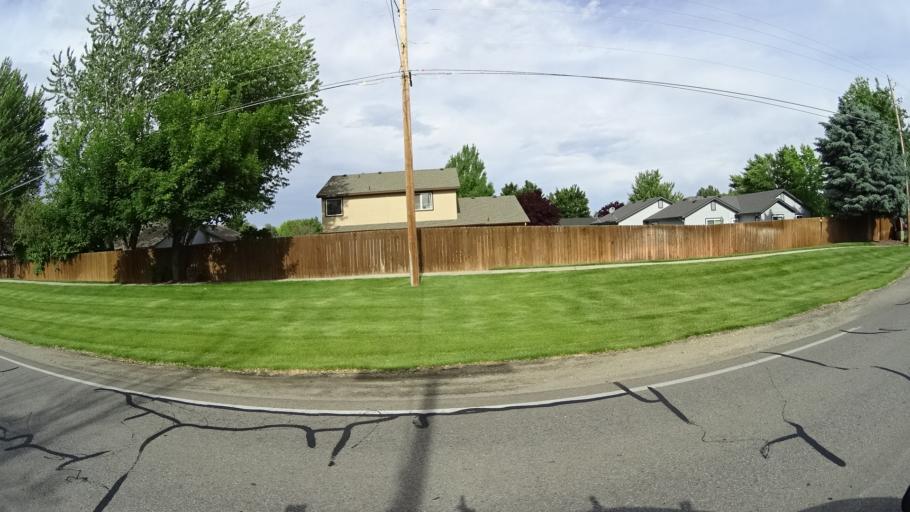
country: US
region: Idaho
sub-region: Ada County
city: Meridian
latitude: 43.5850
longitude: -116.3746
